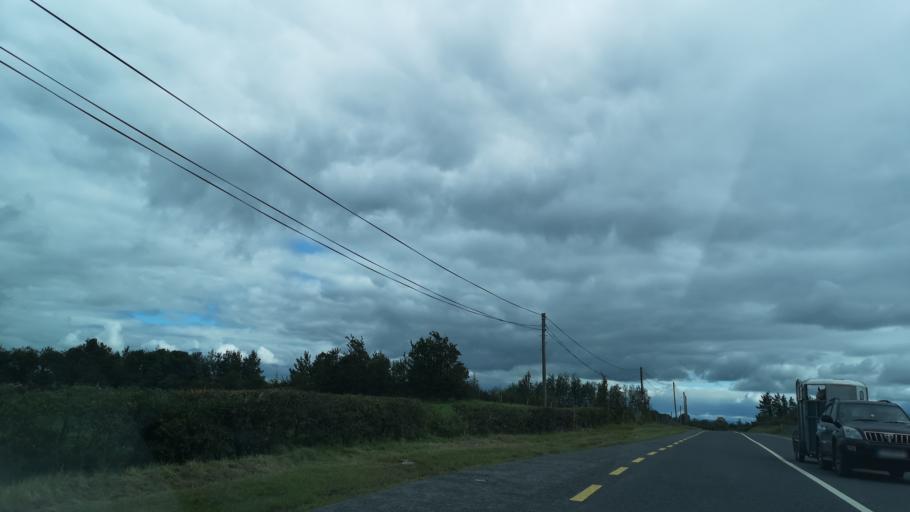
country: IE
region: Connaught
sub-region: County Galway
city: Ballinasloe
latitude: 53.3057
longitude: -8.1421
